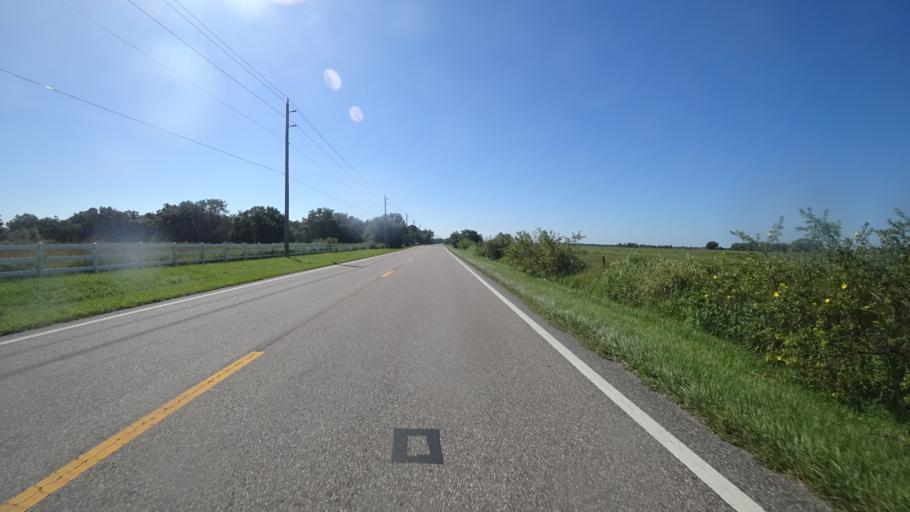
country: US
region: Florida
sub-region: Sarasota County
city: Lake Sarasota
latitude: 27.3542
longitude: -82.2686
